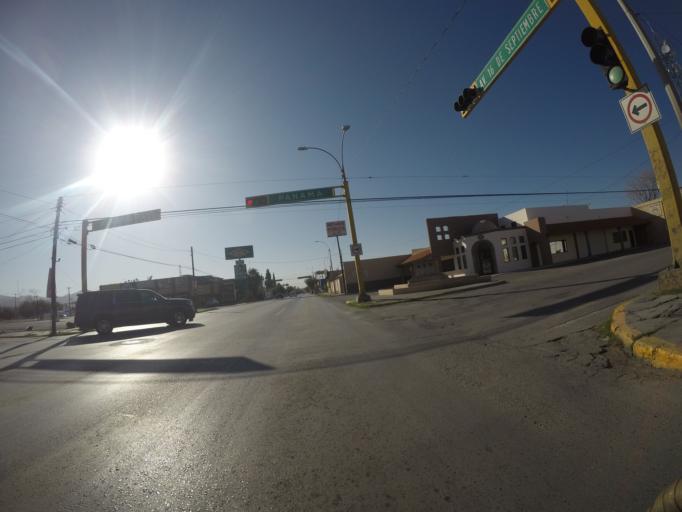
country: MX
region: Chihuahua
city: Ciudad Juarez
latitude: 31.7380
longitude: -106.4642
